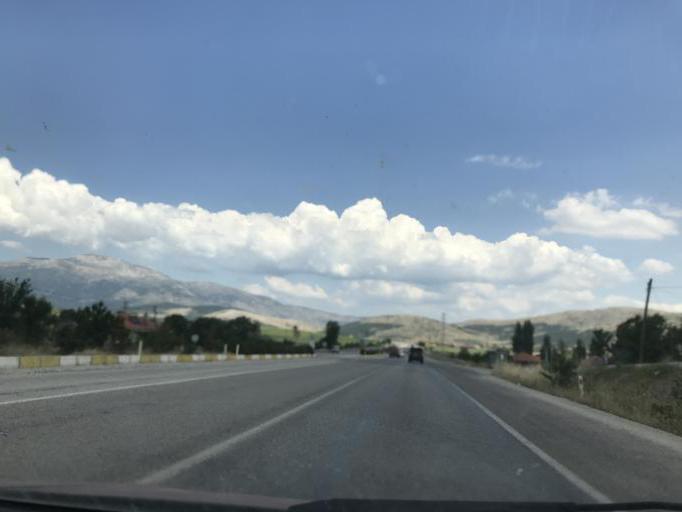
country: TR
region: Denizli
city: Serinhisar
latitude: 37.6159
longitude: 29.1724
